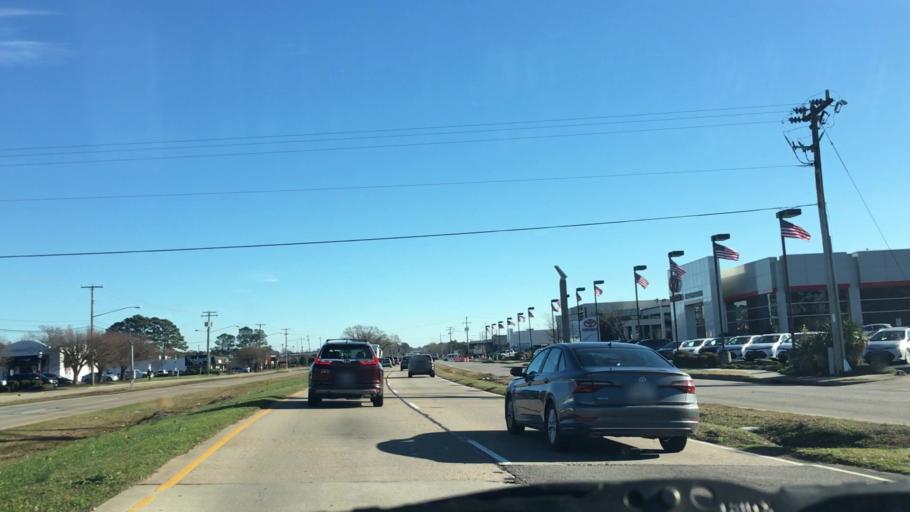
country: US
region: Virginia
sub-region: City of Virginia Beach
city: Virginia Beach
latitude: 36.8487
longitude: -76.0323
